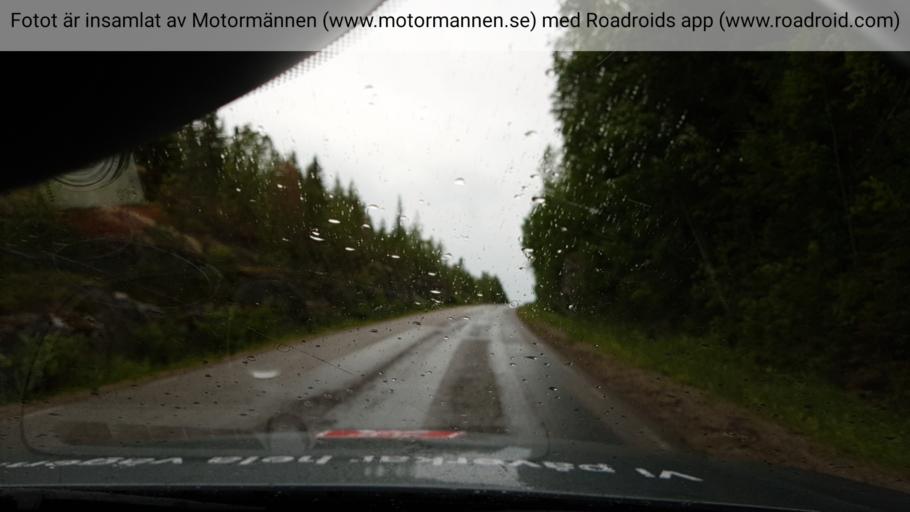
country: SE
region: Jaemtland
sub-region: Braecke Kommun
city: Braecke
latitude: 62.3685
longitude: 15.1762
